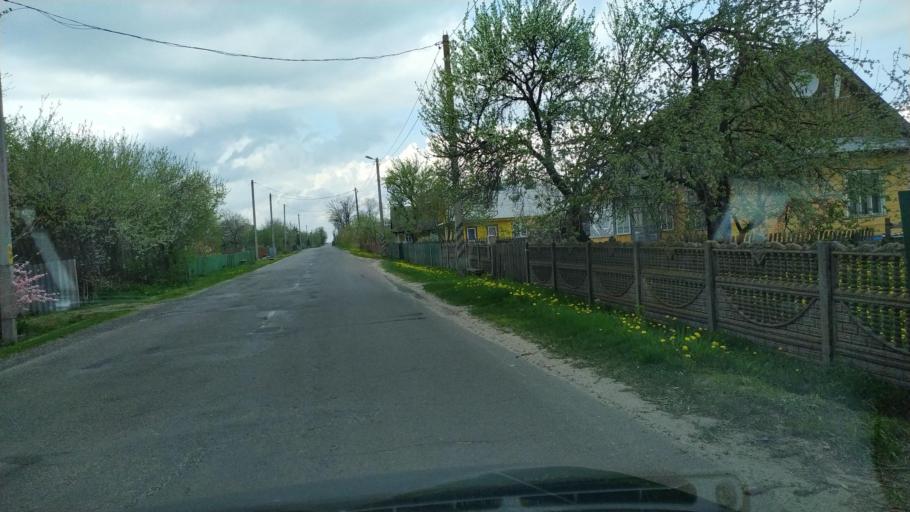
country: BY
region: Brest
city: Pruzhany
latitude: 52.6263
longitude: 24.3889
